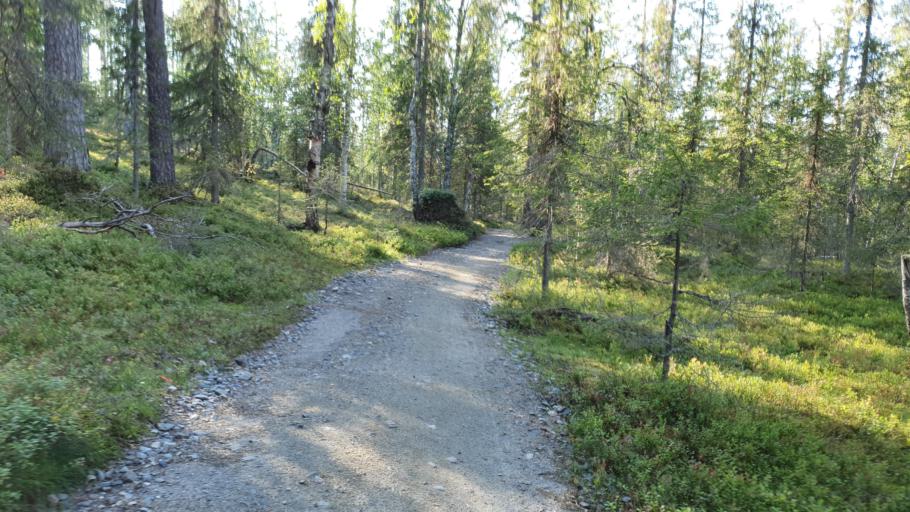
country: FI
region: Lapland
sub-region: Tunturi-Lappi
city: Kolari
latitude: 67.5979
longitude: 24.2160
